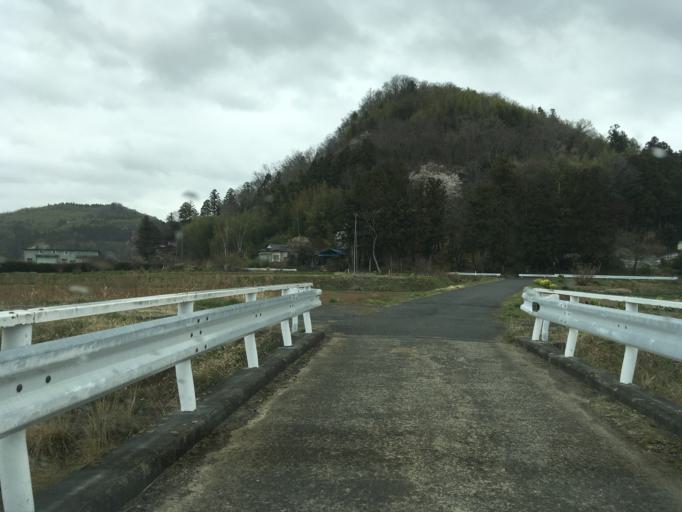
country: JP
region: Iwate
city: Ichinoseki
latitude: 38.7484
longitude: 141.2191
